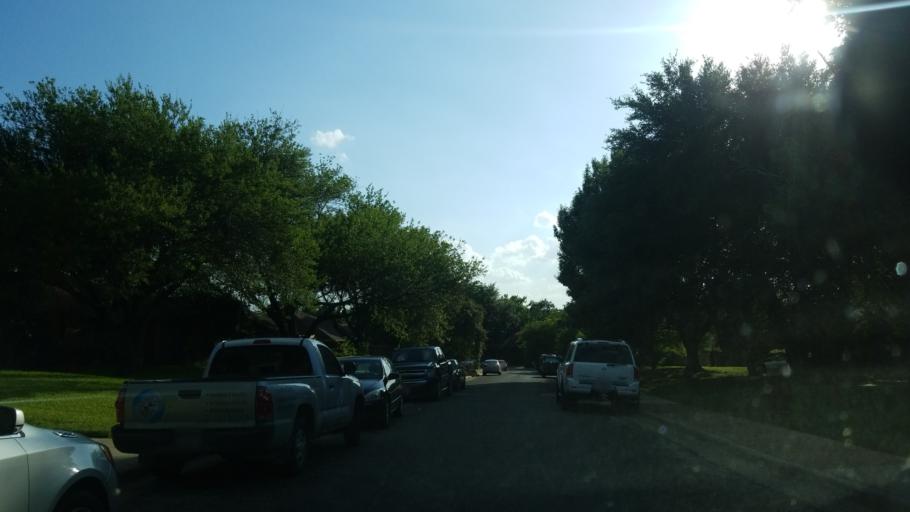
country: US
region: Texas
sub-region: Dallas County
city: Highland Park
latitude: 32.7824
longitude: -96.7080
